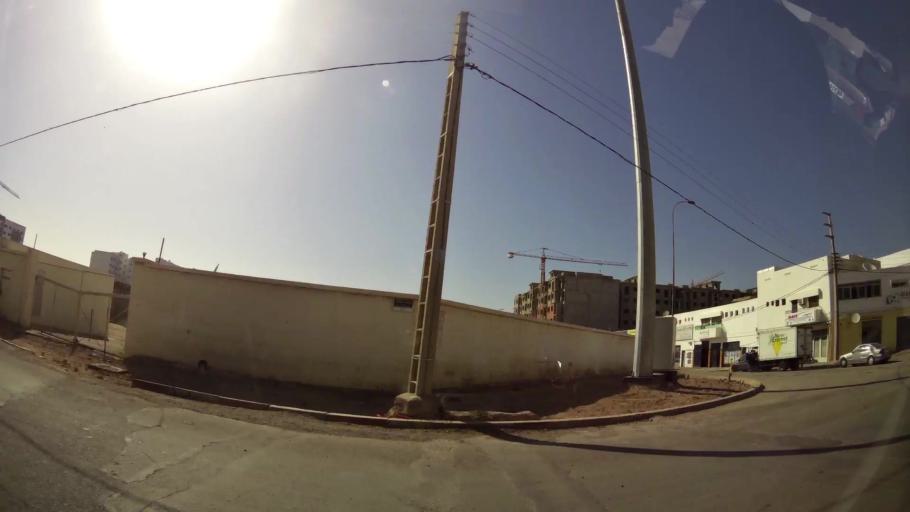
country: MA
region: Oued ed Dahab-Lagouira
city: Dakhla
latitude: 30.4196
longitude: -9.5750
